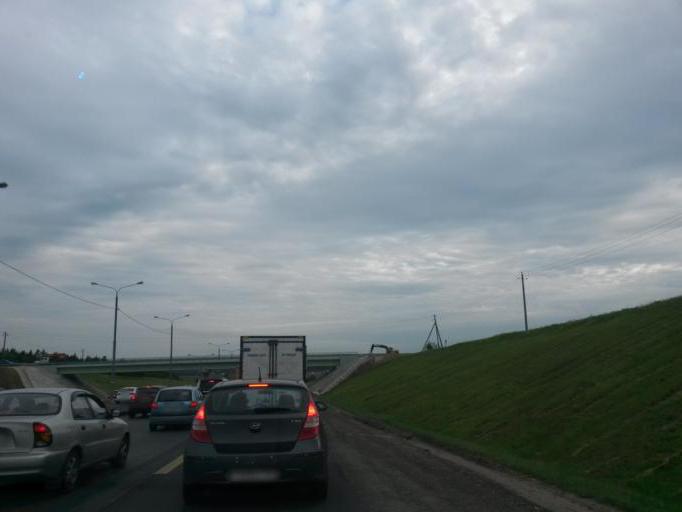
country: RU
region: Moskovskaya
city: Klimovsk
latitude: 55.3528
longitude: 37.5935
